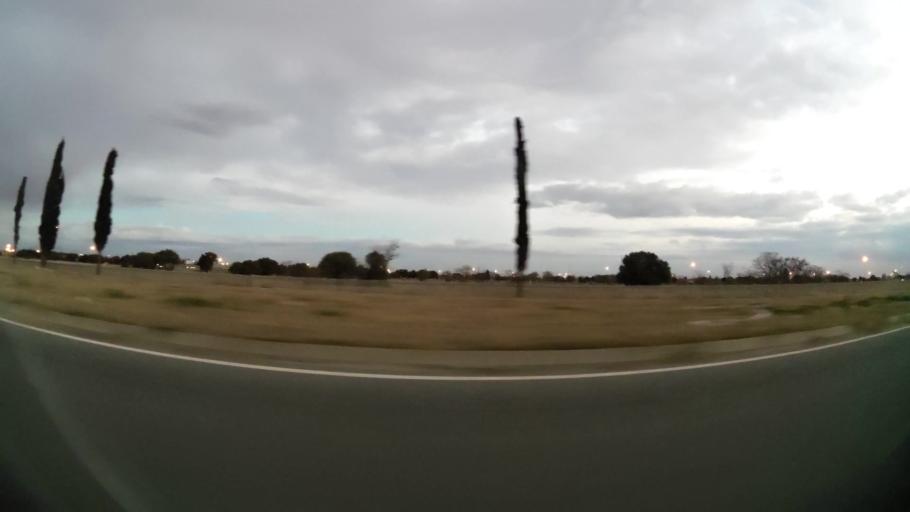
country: ZA
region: Orange Free State
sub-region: Lejweleputswa District Municipality
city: Welkom
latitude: -27.9495
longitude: 26.7957
